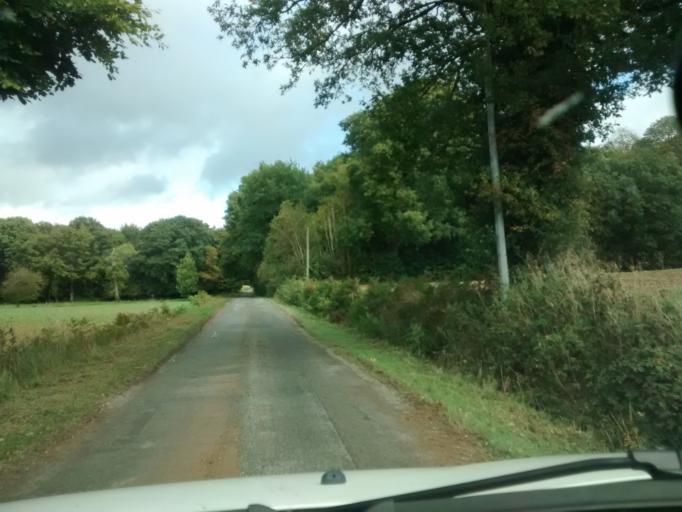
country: FR
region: Brittany
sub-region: Departement d'Ille-et-Vilaine
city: Chateaubourg
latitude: 48.1373
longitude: -1.4164
